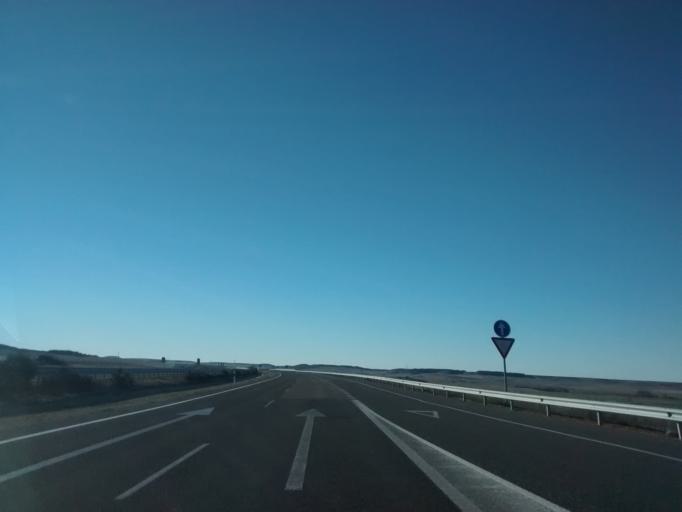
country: ES
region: Castille and Leon
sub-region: Provincia de Palencia
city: Pradanos de Ojeda
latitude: 42.6527
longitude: -4.3494
